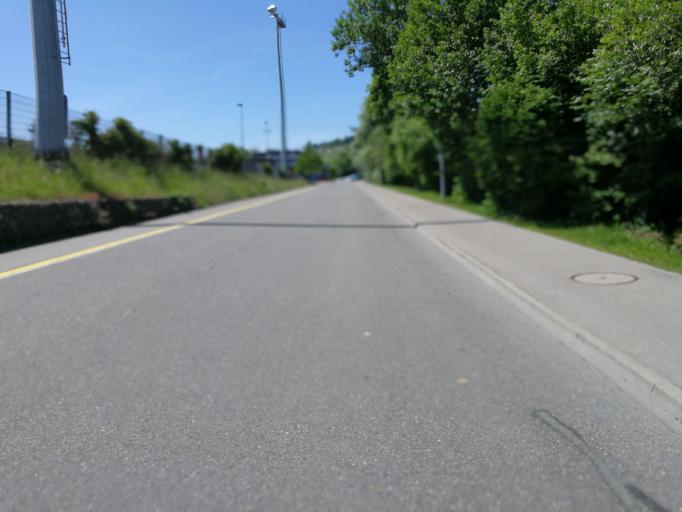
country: CH
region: Schwyz
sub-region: Bezirk Hoefe
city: Freienbach
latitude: 47.2001
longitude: 8.7544
